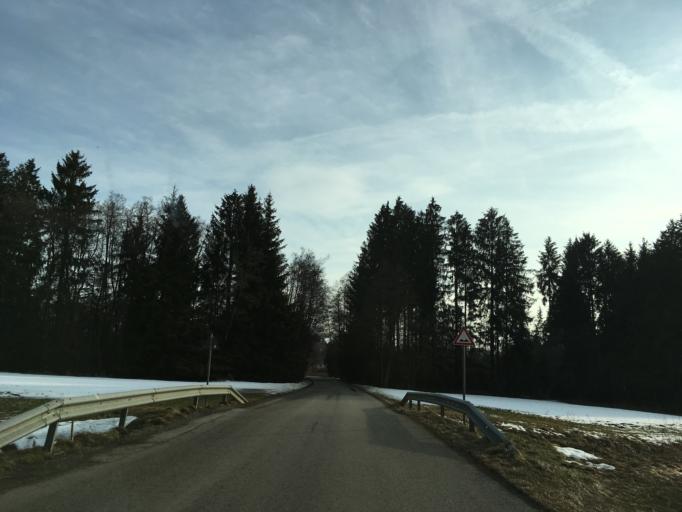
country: DE
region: Bavaria
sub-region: Upper Bavaria
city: Sochtenau
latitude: 47.9515
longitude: 12.2187
